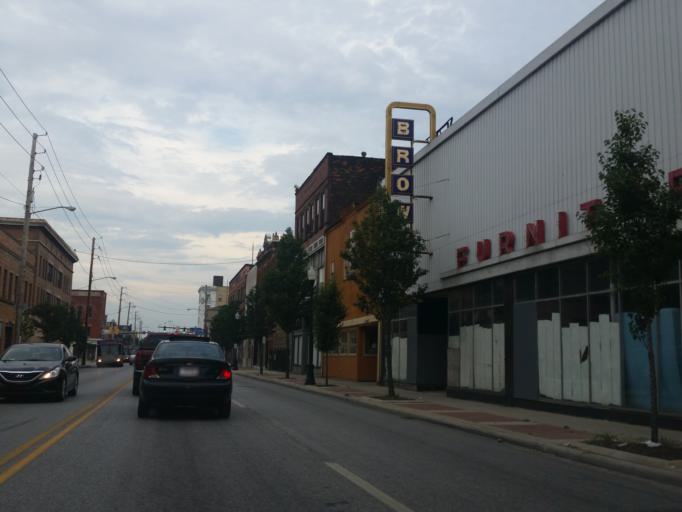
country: US
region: Ohio
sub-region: Cuyahoga County
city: Newburgh Heights
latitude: 41.4680
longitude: -81.6524
